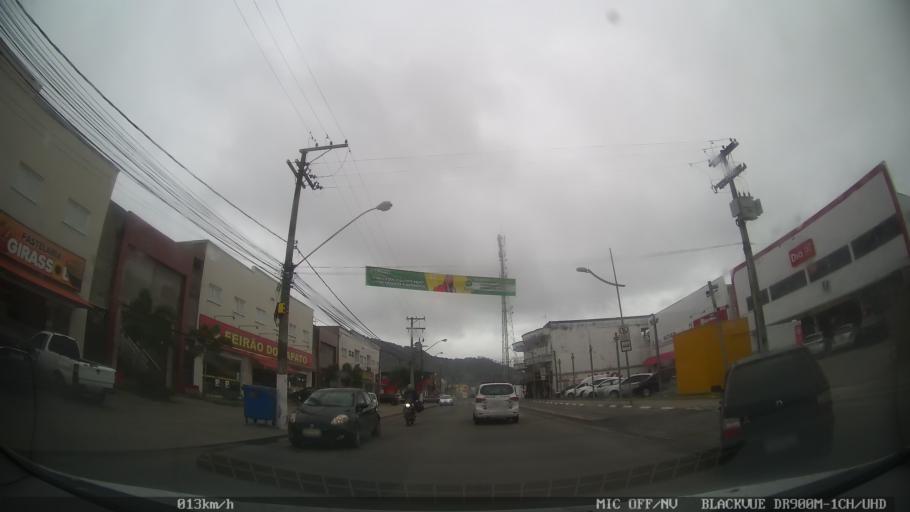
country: BR
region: Sao Paulo
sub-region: Juquia
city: Juquia
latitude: -24.3208
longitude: -47.6368
